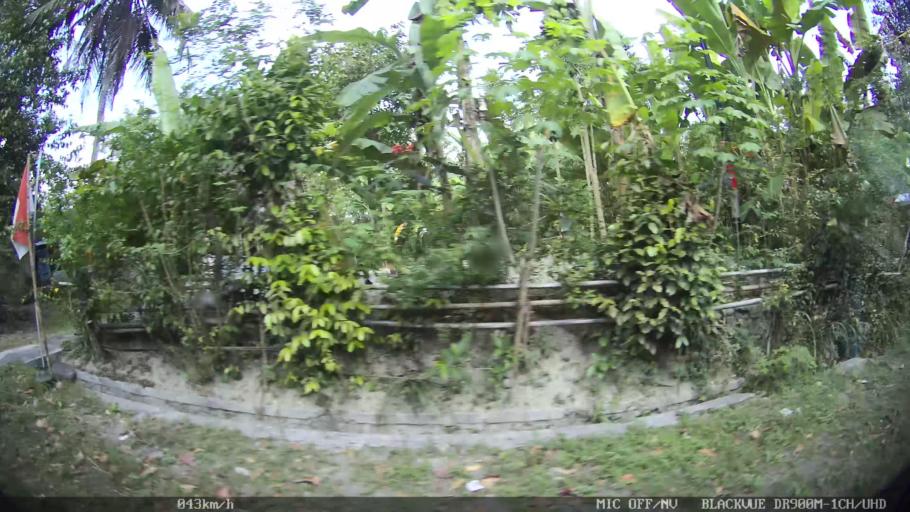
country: ID
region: Daerah Istimewa Yogyakarta
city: Bantul
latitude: -7.8614
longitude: 110.3194
